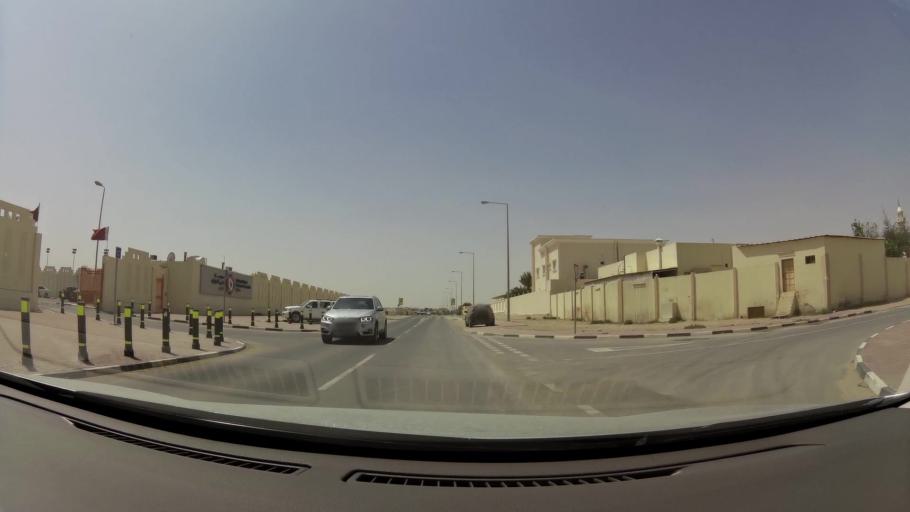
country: QA
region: Baladiyat Umm Salal
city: Umm Salal Muhammad
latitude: 25.3991
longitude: 51.4498
